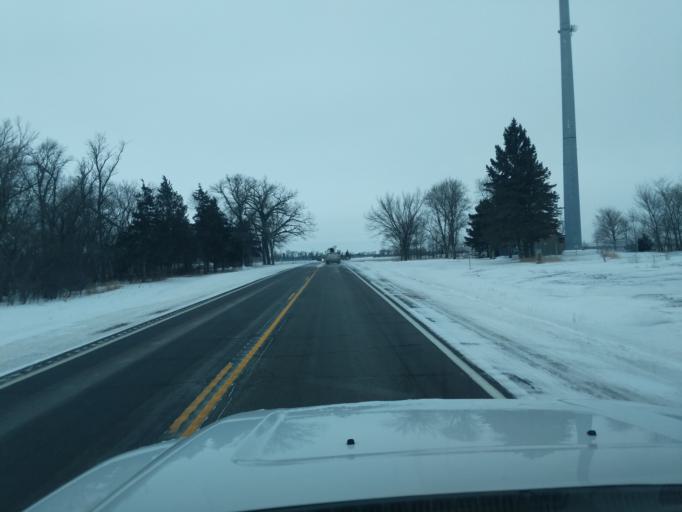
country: US
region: Minnesota
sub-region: Redwood County
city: Redwood Falls
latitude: 44.5989
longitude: -94.9944
